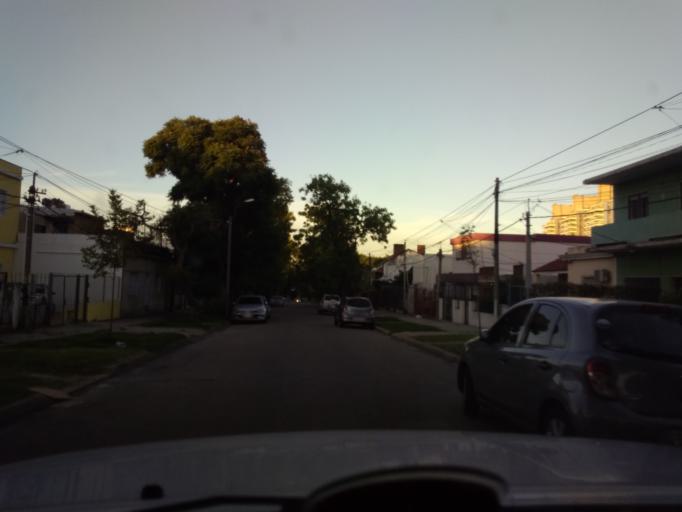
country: UY
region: Montevideo
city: Montevideo
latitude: -34.8957
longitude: -56.1252
